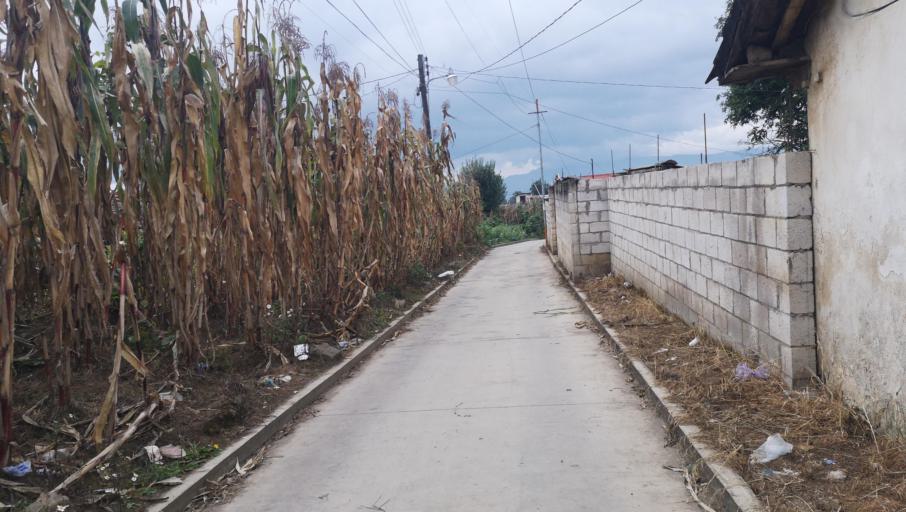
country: GT
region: Quetzaltenango
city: Cantel
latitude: 14.8190
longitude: -91.4350
